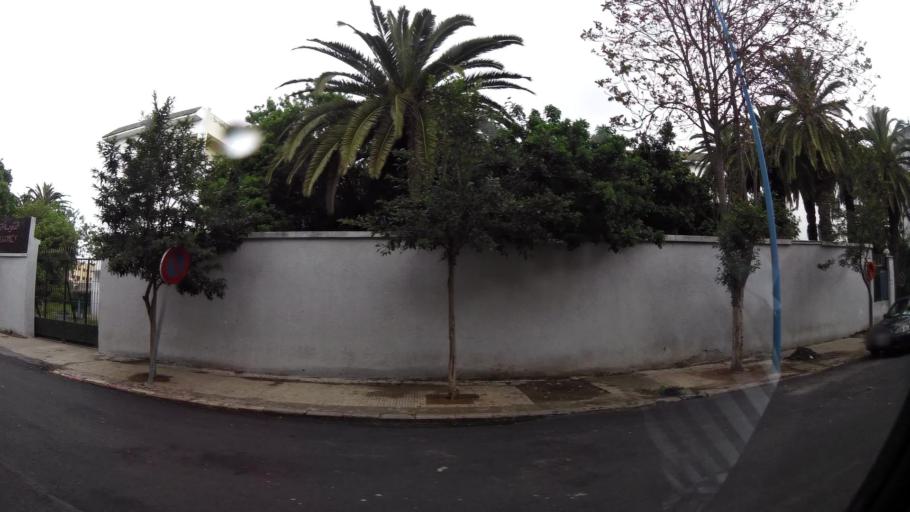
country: MA
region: Grand Casablanca
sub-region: Casablanca
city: Casablanca
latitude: 33.5793
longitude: -7.5993
